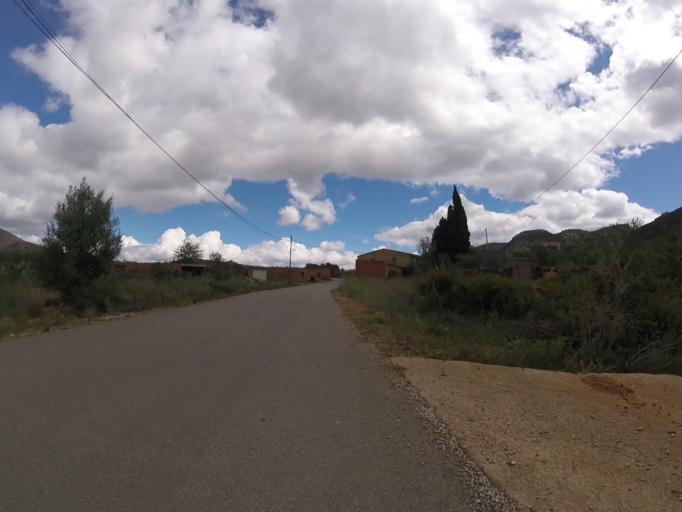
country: ES
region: Valencia
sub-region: Provincia de Castello
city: Sierra-Engarceran
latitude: 40.2957
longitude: -0.0443
